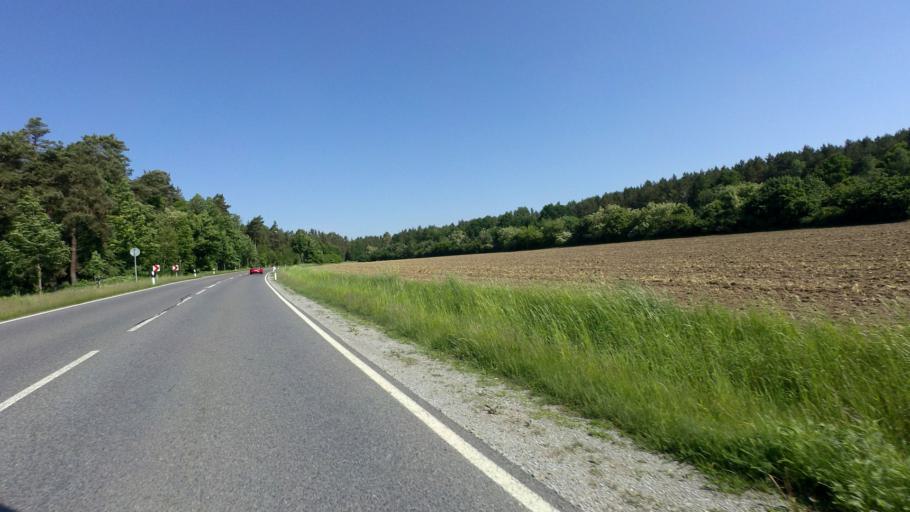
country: DE
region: Saxony
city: Kamenz
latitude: 51.3044
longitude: 14.0939
